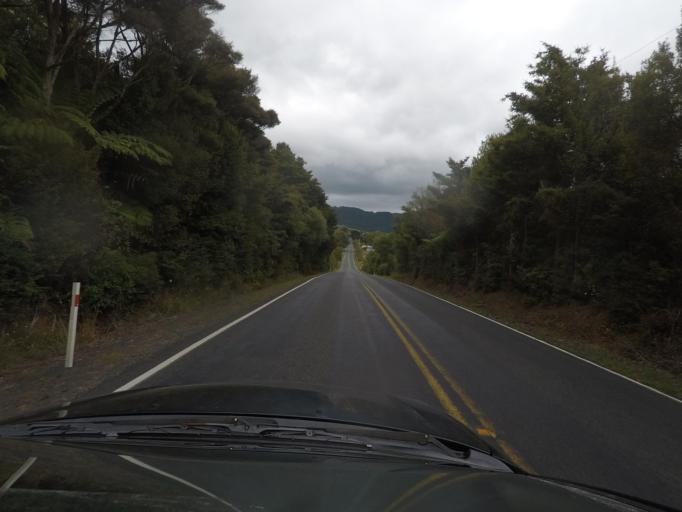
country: NZ
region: Auckland
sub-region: Auckland
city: Wellsford
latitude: -36.2825
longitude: 174.6363
